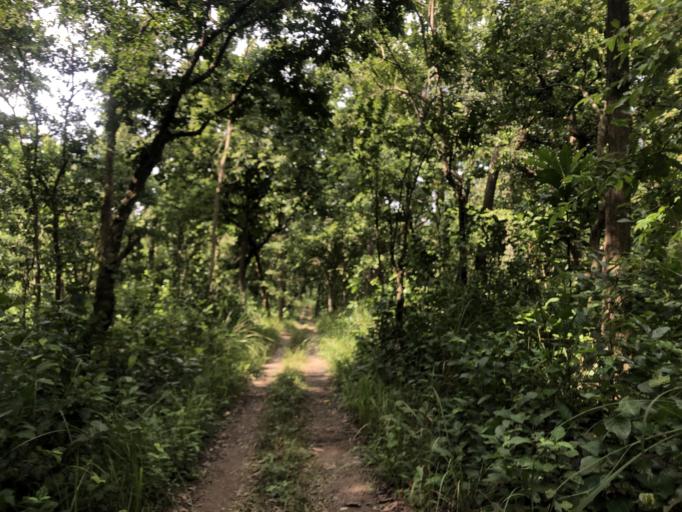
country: NP
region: Far Western
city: Tikapur
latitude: 28.5442
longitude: 81.2864
